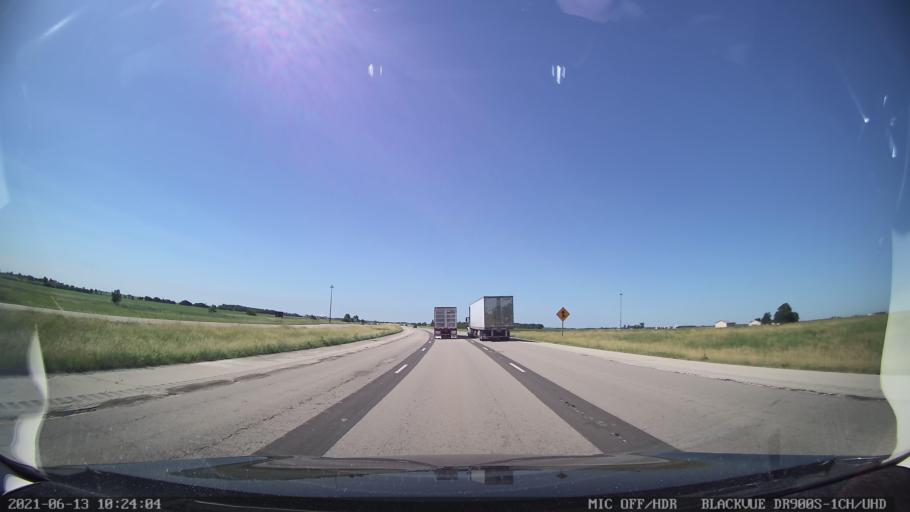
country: US
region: Illinois
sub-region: Sangamon County
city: Williamsville
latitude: 40.0185
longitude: -89.4979
